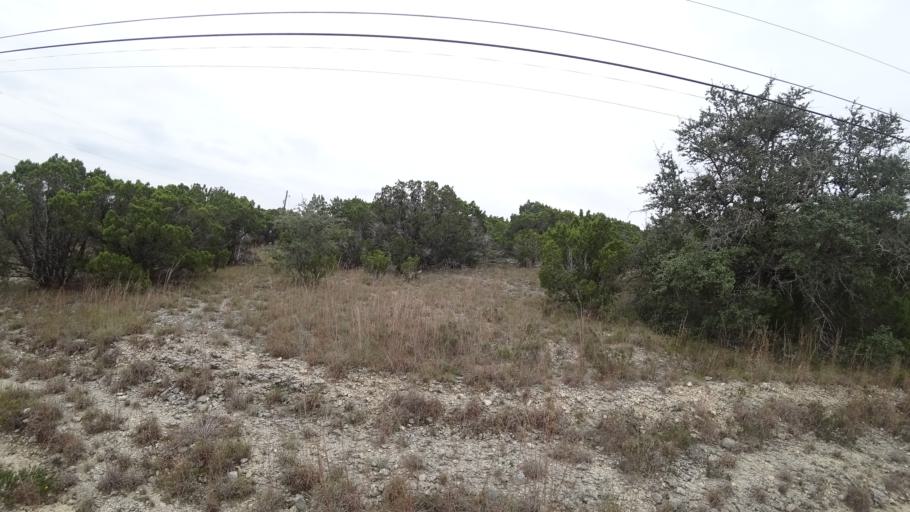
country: US
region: Texas
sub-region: Travis County
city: Lakeway
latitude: 30.3723
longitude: -97.9407
